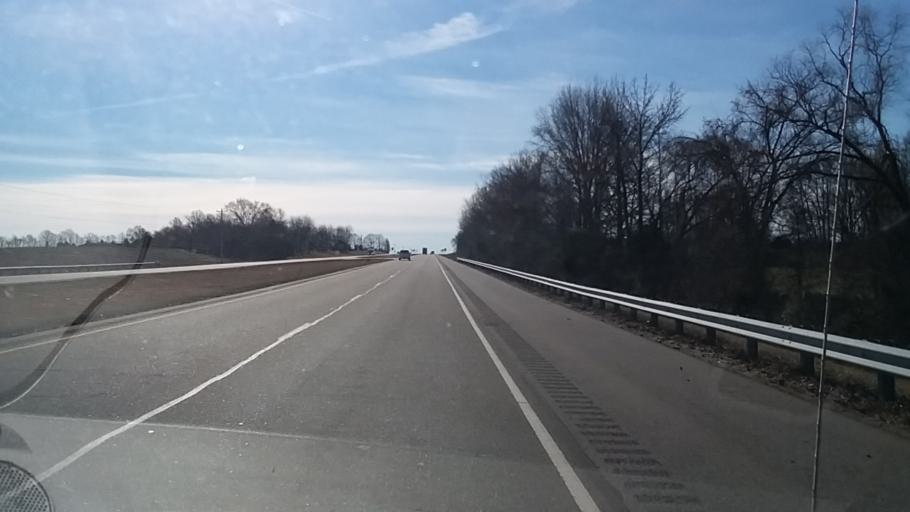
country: US
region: Tennessee
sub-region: Lauderdale County
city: Halls
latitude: 35.8965
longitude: -89.2434
